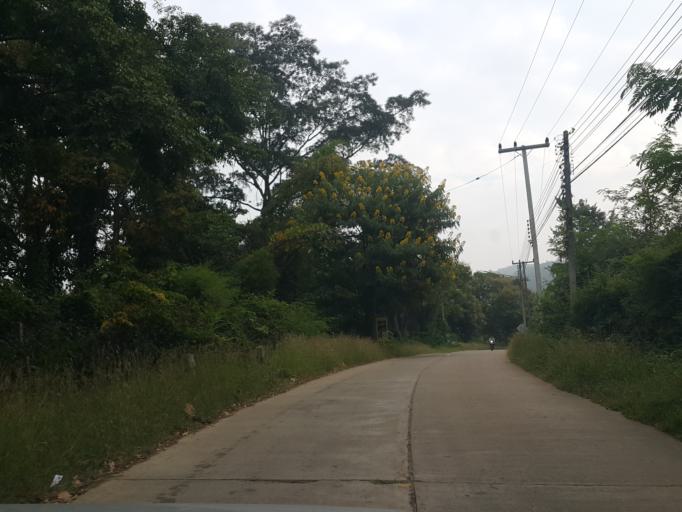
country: TH
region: Chiang Mai
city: Pai
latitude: 19.3570
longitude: 98.4463
